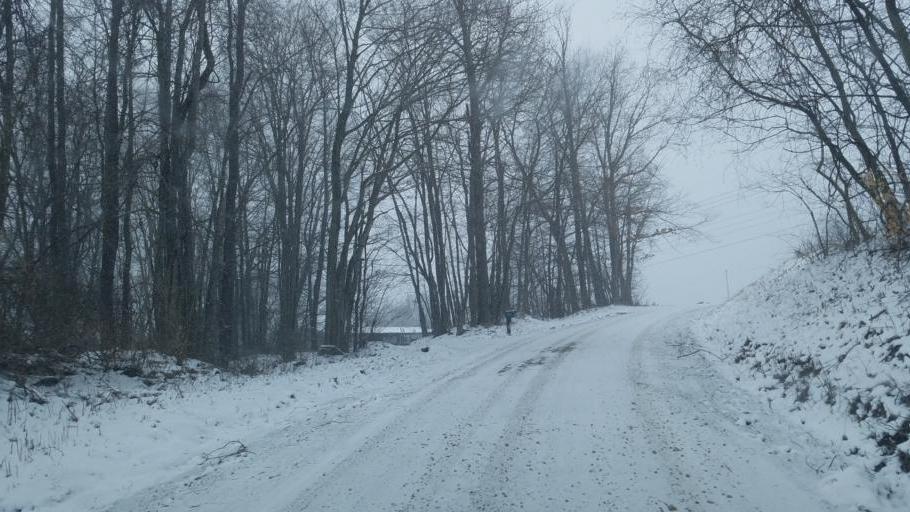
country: US
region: Pennsylvania
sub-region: Venango County
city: Sugarcreek
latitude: 41.4724
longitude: -79.9420
